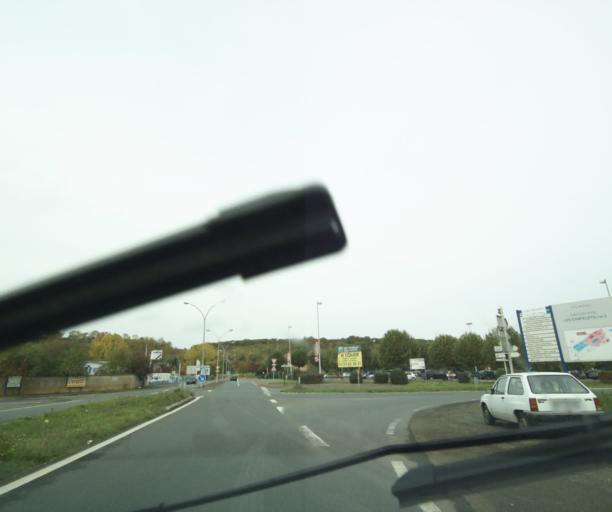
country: FR
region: Centre
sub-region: Departement d'Eure-et-Loir
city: Dreux
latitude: 48.7477
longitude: 1.3890
